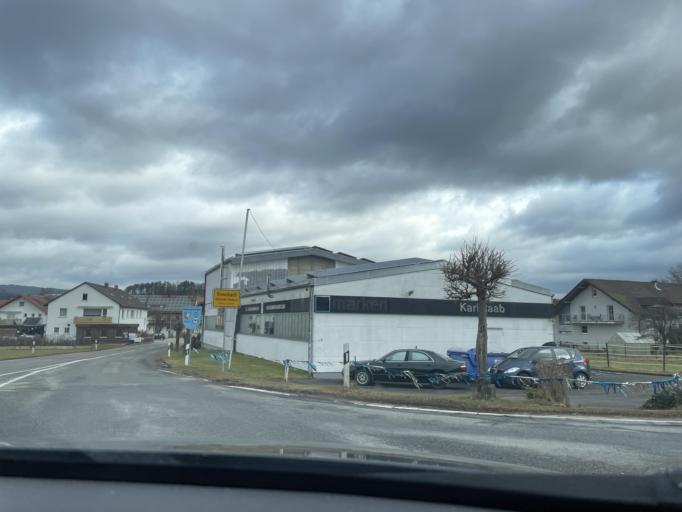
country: DE
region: Bavaria
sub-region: Upper Palatinate
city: Blaibach
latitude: 49.1593
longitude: 12.8063
